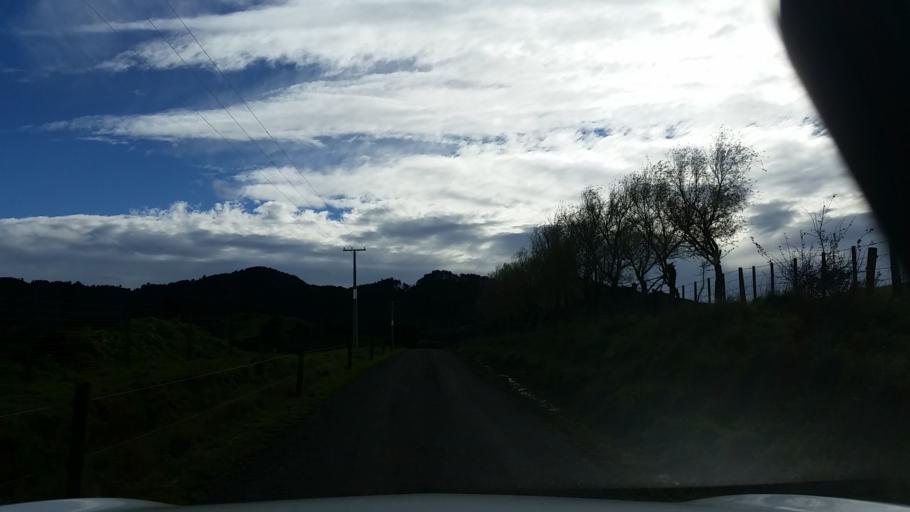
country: NZ
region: Waikato
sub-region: Hauraki District
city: Ngatea
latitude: -37.4997
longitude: 175.4041
